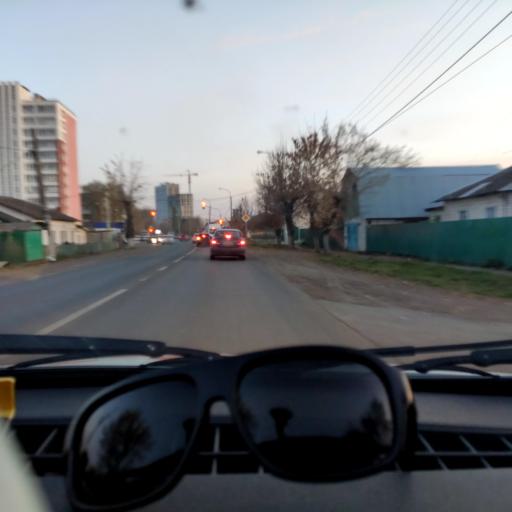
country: RU
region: Bashkortostan
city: Avdon
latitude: 54.7023
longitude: 55.8221
